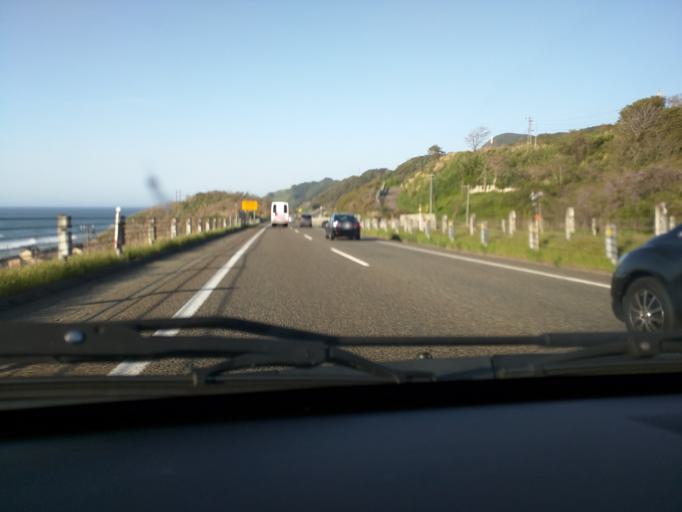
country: JP
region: Niigata
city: Kashiwazaki
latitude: 37.3074
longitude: 138.4216
